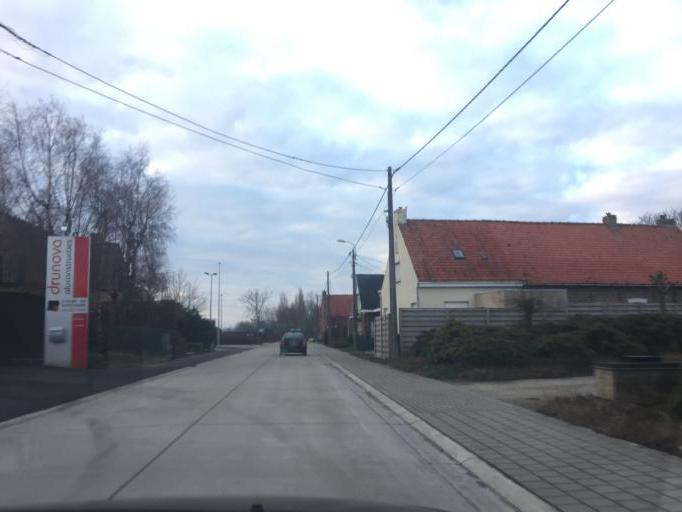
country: BE
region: Flanders
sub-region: Provincie West-Vlaanderen
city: Hooglede
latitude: 50.9713
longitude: 3.0771
